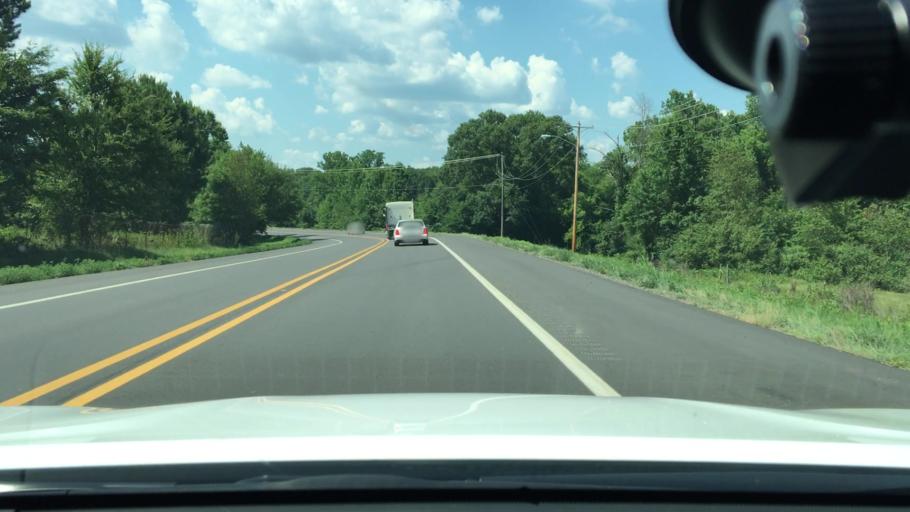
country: US
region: Arkansas
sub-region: Johnson County
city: Clarksville
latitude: 35.4499
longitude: -93.5291
